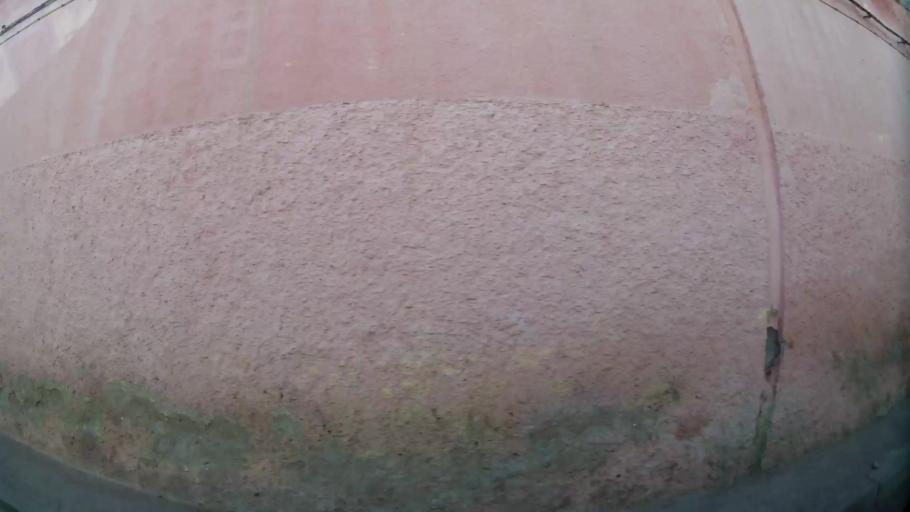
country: MA
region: Oriental
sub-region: Oujda-Angad
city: Oujda
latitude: 34.6737
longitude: -1.9278
